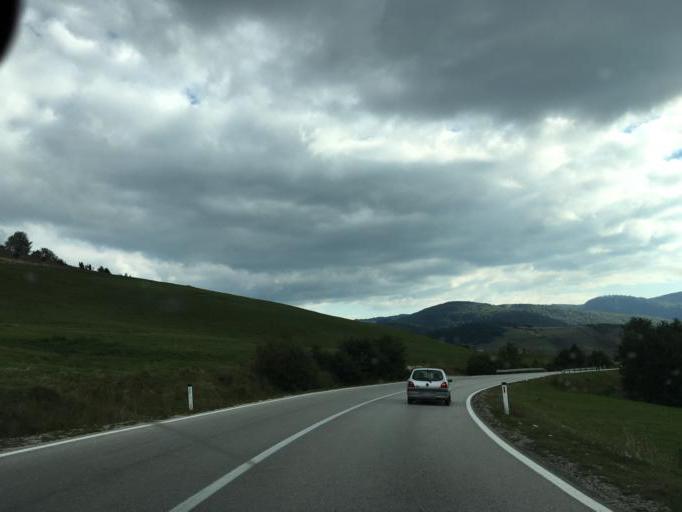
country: BA
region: Federation of Bosnia and Herzegovina
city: Novi Travnik
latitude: 44.1142
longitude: 17.5762
